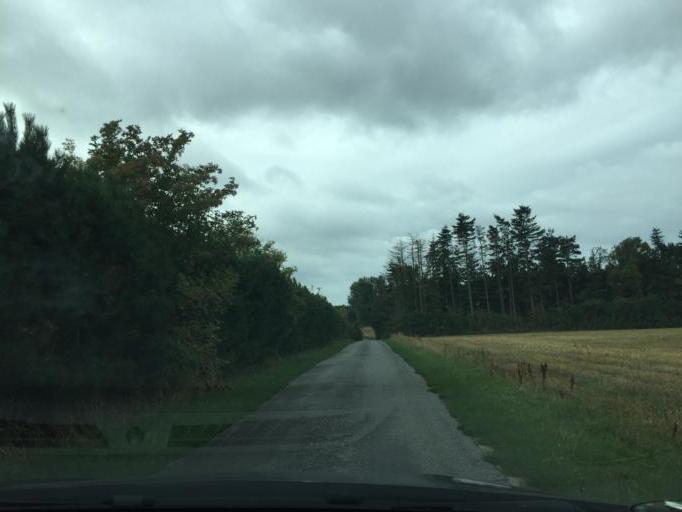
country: DK
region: South Denmark
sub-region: Assens Kommune
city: Harby
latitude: 55.1961
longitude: 10.1439
